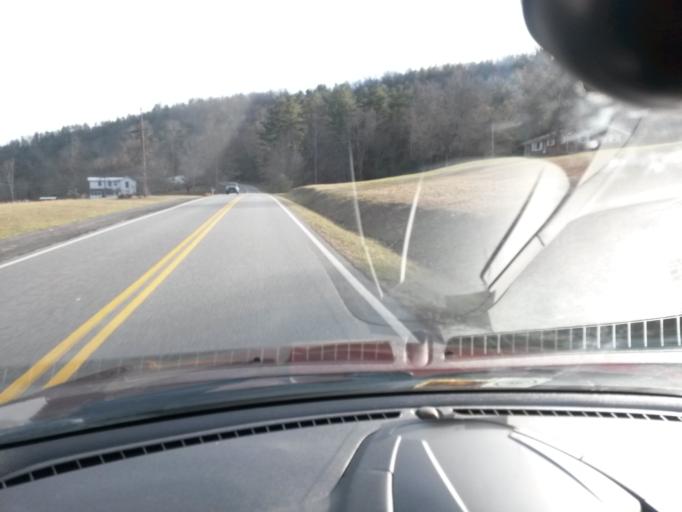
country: US
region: Virginia
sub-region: Alleghany County
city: Clifton Forge
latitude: 37.8802
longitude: -79.7503
